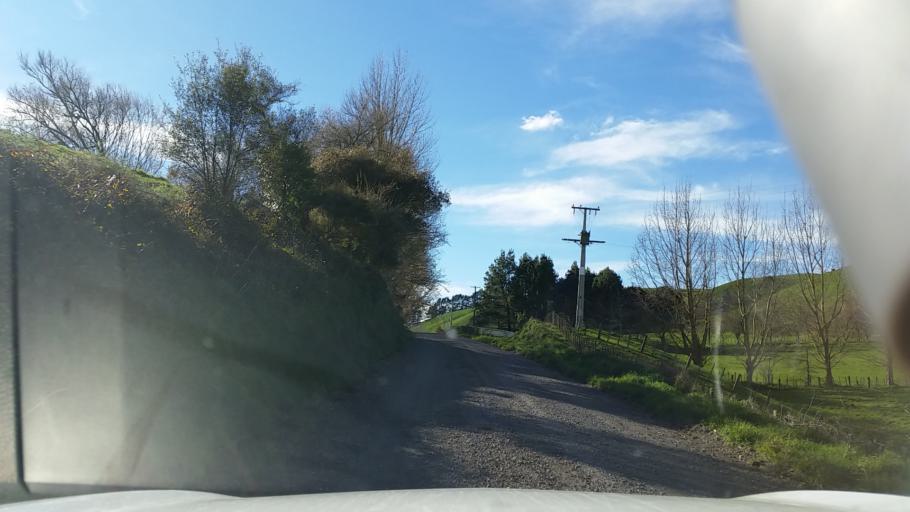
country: NZ
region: Bay of Plenty
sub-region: Rotorua District
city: Rotorua
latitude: -38.3596
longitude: 176.2259
